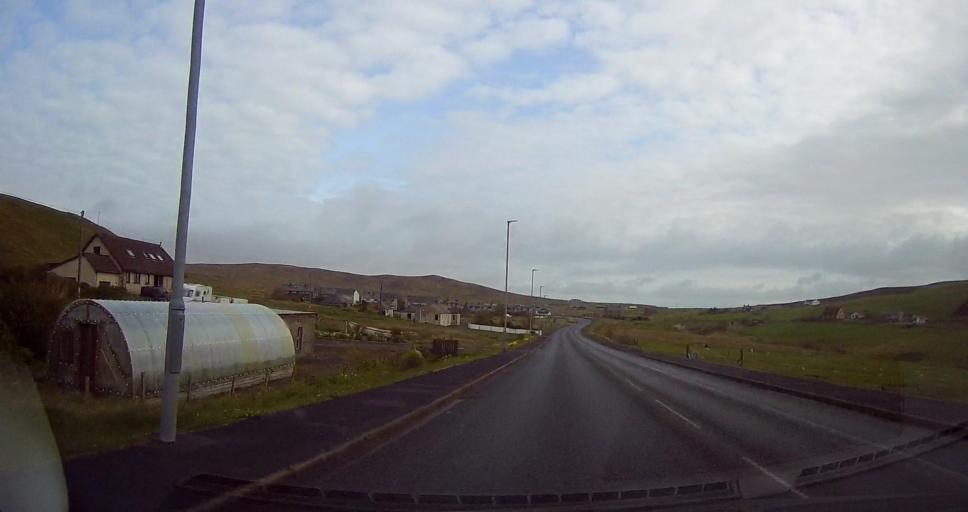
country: GB
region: Scotland
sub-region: Shetland Islands
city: Sandwick
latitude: 60.0501
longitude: -1.2271
